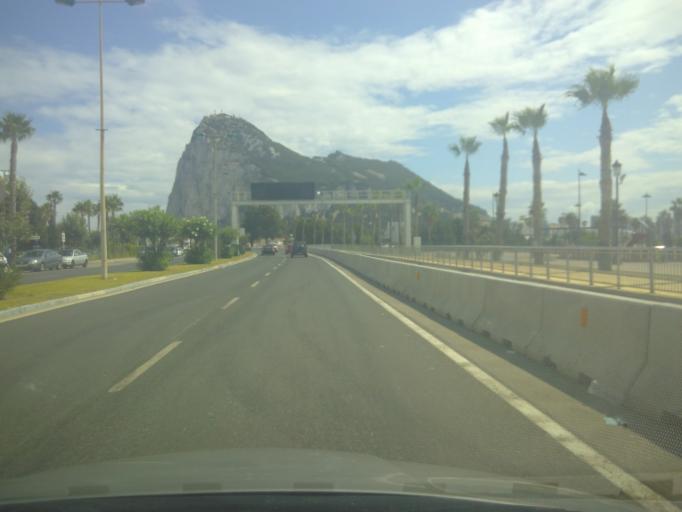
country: ES
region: Andalusia
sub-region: Provincia de Cadiz
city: La Linea de la Concepcion
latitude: 36.1580
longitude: -5.3532
